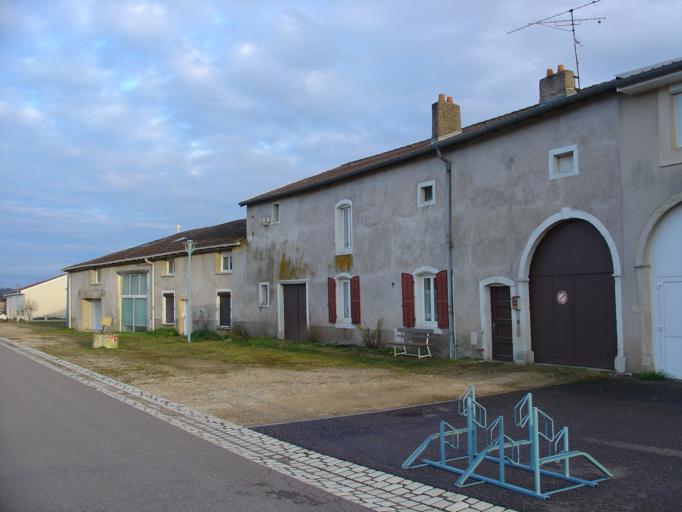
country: FR
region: Lorraine
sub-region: Departement de Meurthe-et-Moselle
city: Villey-Saint-Etienne
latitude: 48.7574
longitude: 5.9686
